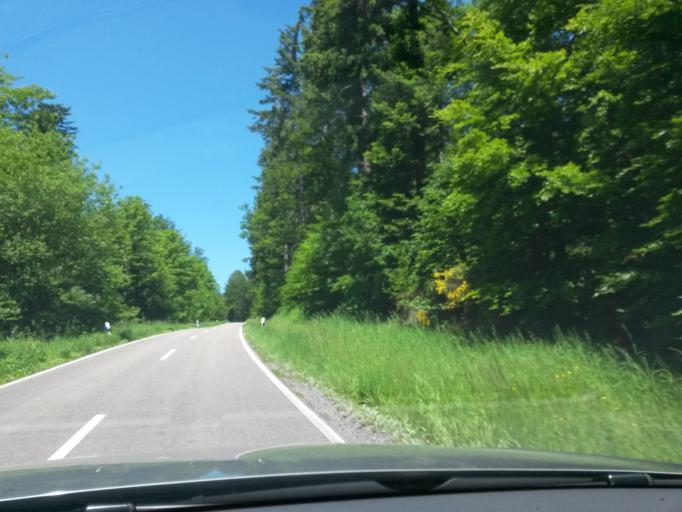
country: DE
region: Baden-Wuerttemberg
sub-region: Karlsruhe Region
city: Tiefenbronn
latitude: 48.8528
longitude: 8.7653
